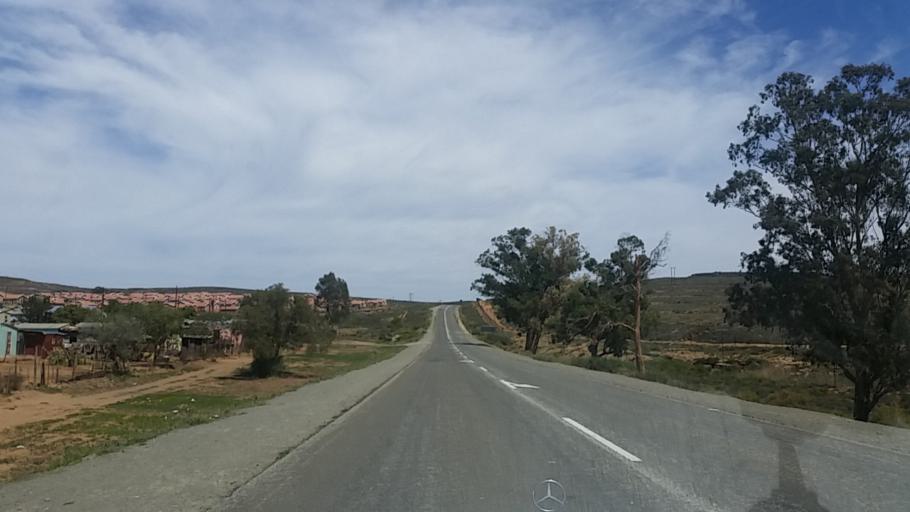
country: ZA
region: Western Cape
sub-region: Eden District Municipality
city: Knysna
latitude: -33.6621
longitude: 23.1095
